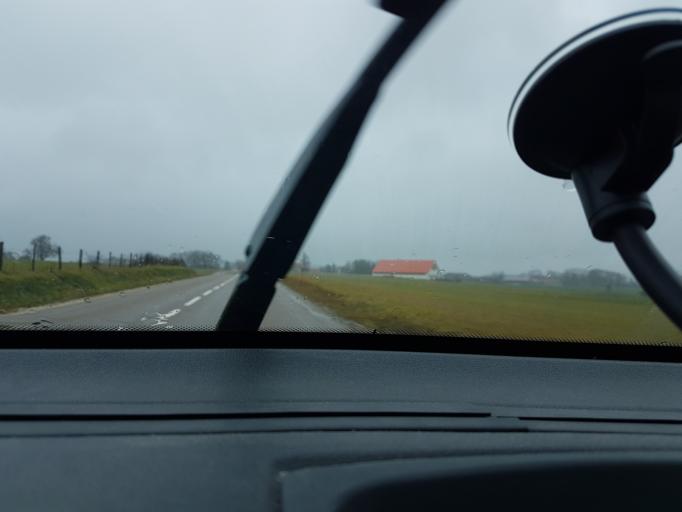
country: FR
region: Franche-Comte
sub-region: Departement du Doubs
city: Valdahon
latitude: 47.1233
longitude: 6.3626
